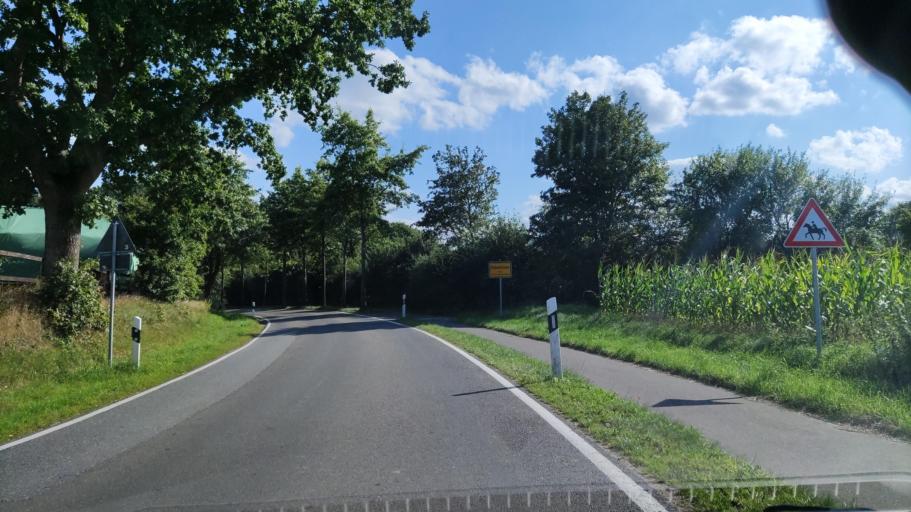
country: DE
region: Schleswig-Holstein
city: Oldenhutten
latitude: 54.1596
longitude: 9.7357
